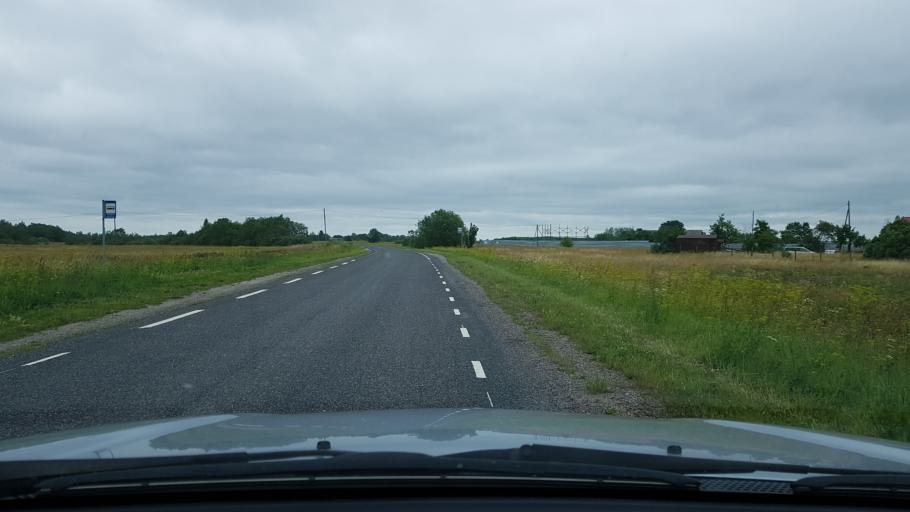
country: EE
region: Ida-Virumaa
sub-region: Narva linn
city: Narva
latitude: 59.3771
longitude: 28.1196
